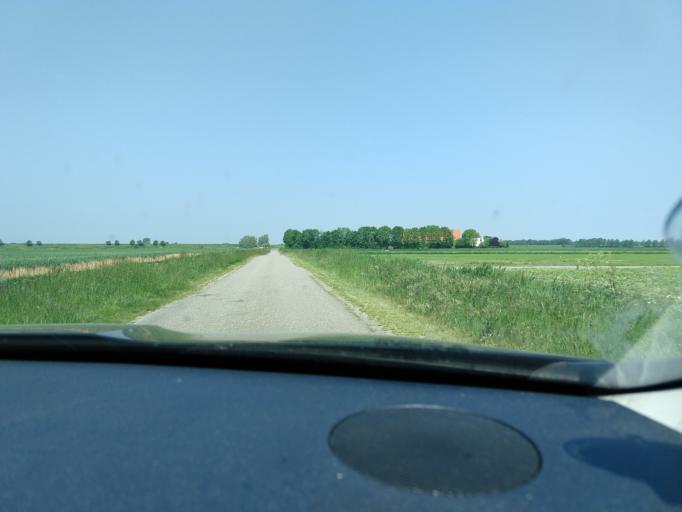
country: NL
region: Zeeland
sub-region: Gemeente Reimerswaal
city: Yerseke
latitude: 51.5679
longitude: 4.0476
